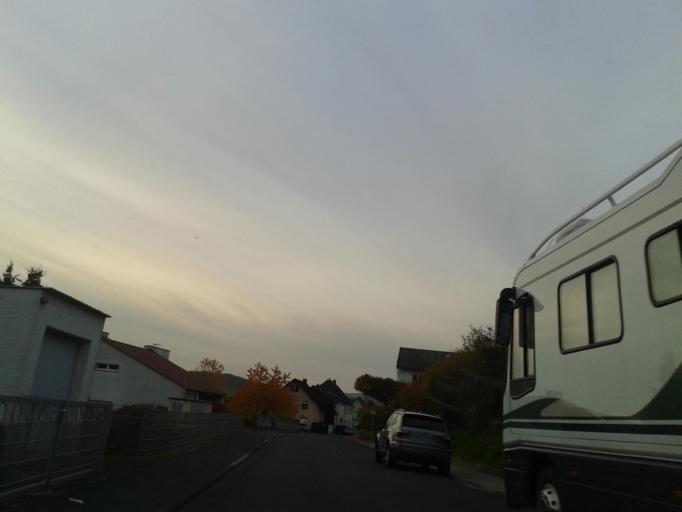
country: DE
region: Hesse
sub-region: Regierungsbezirk Giessen
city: Sinn
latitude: 50.6494
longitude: 8.3362
